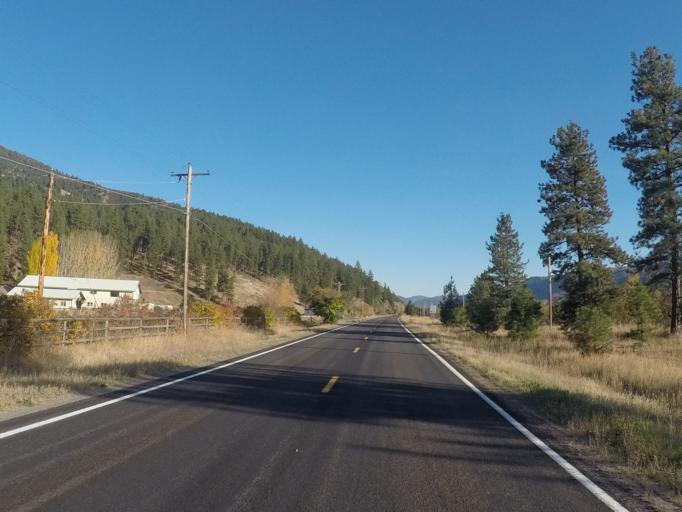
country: US
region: Montana
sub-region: Missoula County
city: Bonner-West Riverside
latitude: 46.8346
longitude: -113.8240
